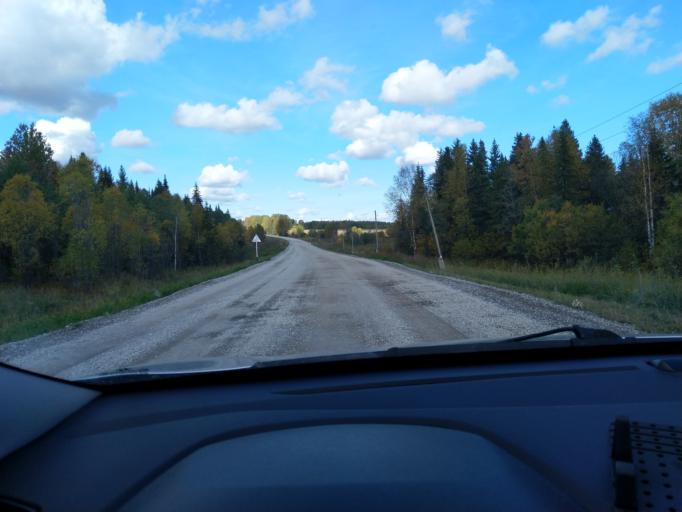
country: RU
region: Perm
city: Usol'ye
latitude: 59.4650
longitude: 56.3701
